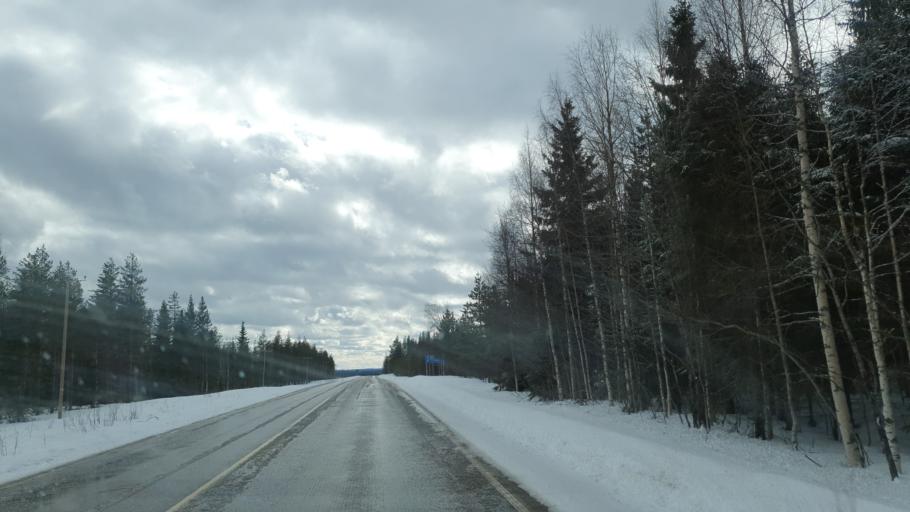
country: FI
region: Kainuu
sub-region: Kehys-Kainuu
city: Puolanka
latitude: 64.9515
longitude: 27.6009
